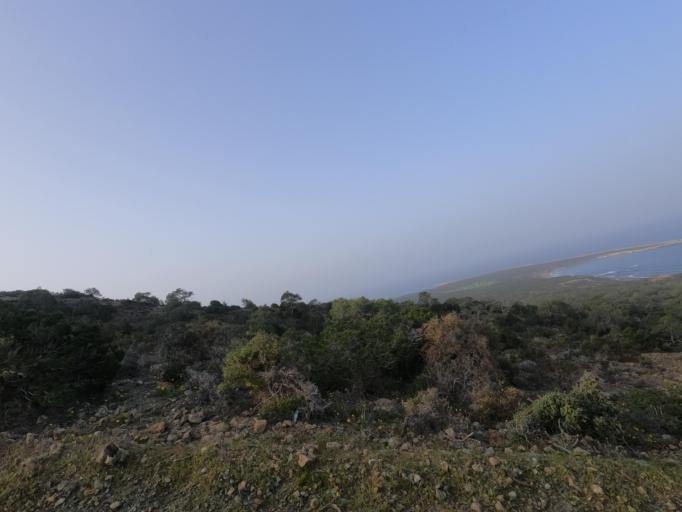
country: CY
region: Pafos
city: Pegeia
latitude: 34.9674
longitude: 32.3242
